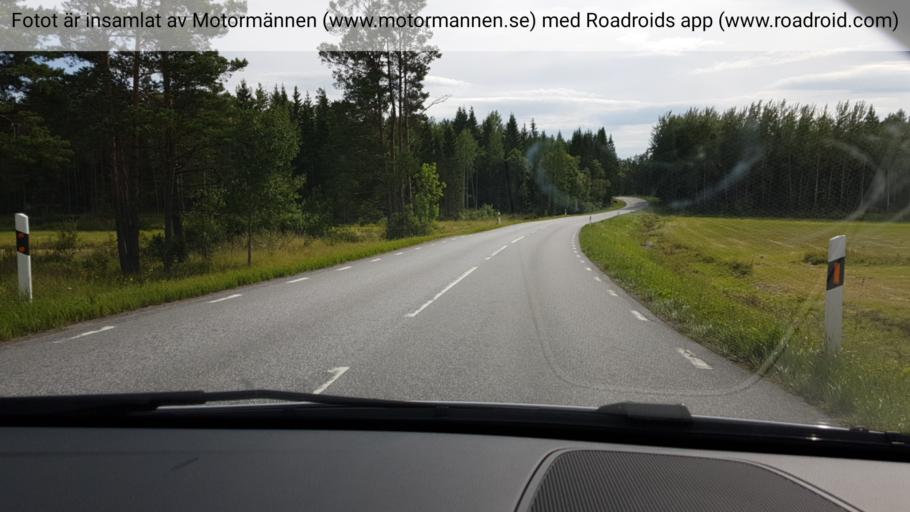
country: SE
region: Uppsala
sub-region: Osthammars Kommun
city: OEsthammar
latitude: 60.2343
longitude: 18.3662
